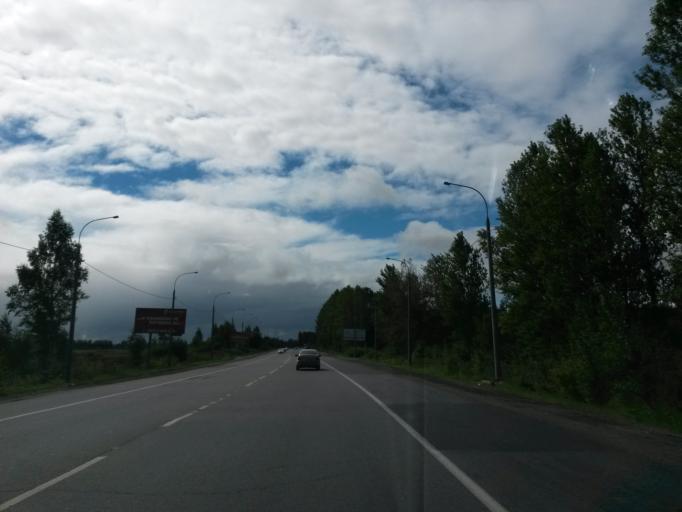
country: RU
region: Jaroslavl
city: Yaroslavl
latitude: 57.6572
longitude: 39.7548
